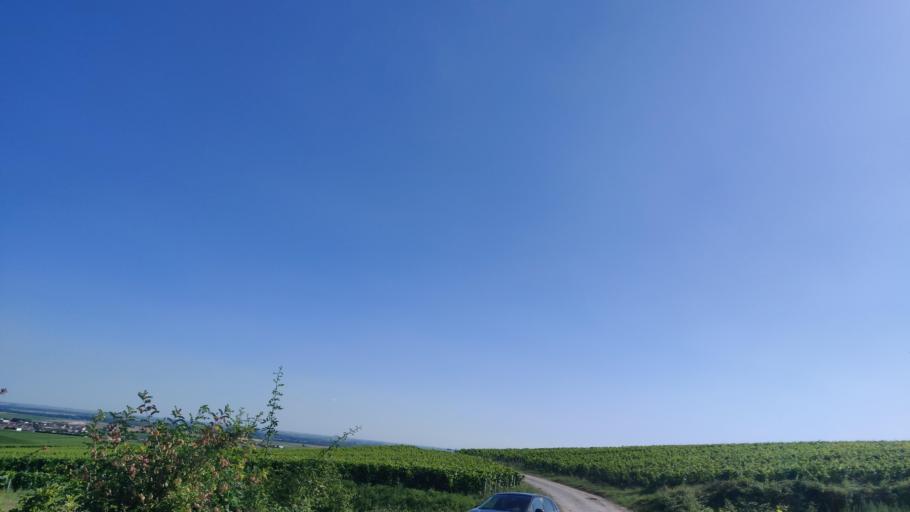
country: FR
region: Champagne-Ardenne
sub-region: Departement de la Marne
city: Tours-sur-Marne
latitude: 49.0937
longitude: 4.1371
